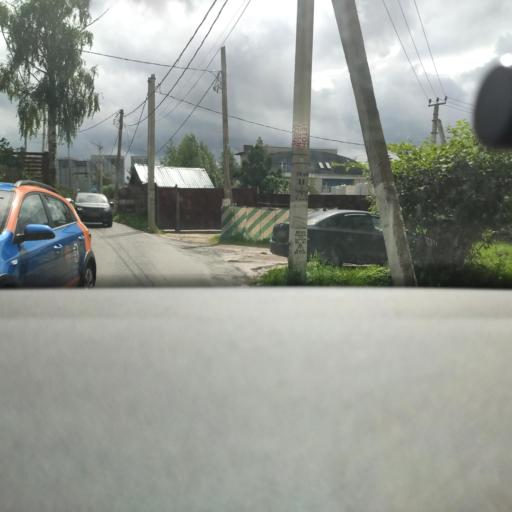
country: RU
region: Moskovskaya
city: Pavshino
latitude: 55.8074
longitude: 37.3766
